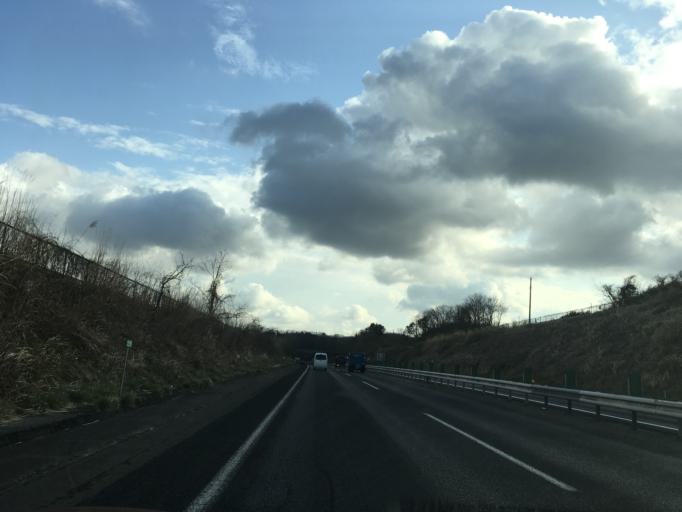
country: JP
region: Miyagi
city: Furukawa
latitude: 38.4993
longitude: 140.9280
